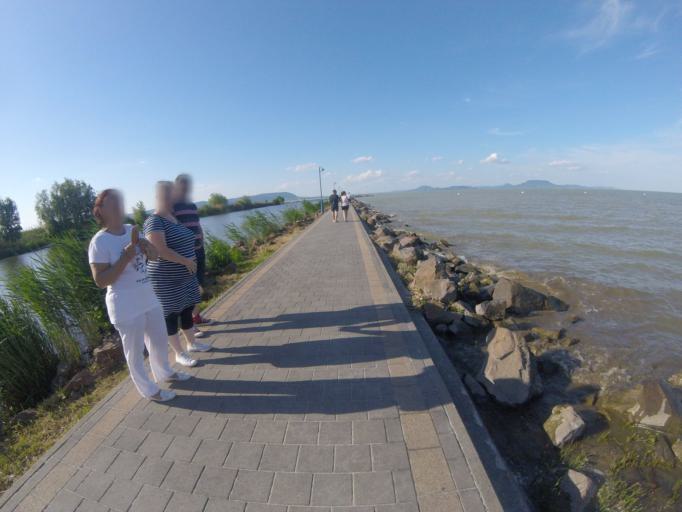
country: HU
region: Somogy
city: Balatonbereny
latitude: 46.7073
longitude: 17.3821
